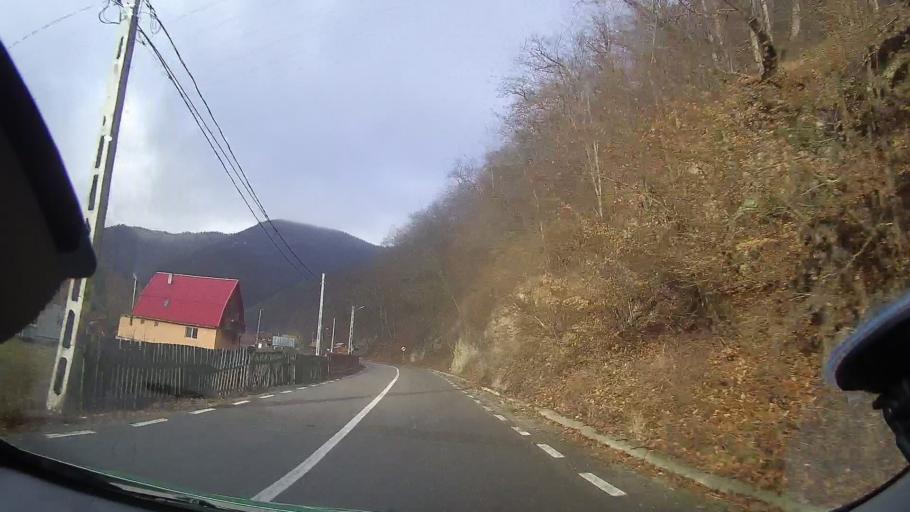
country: RO
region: Cluj
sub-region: Comuna Valea Ierii
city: Valea Ierii
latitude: 46.6442
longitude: 23.3515
